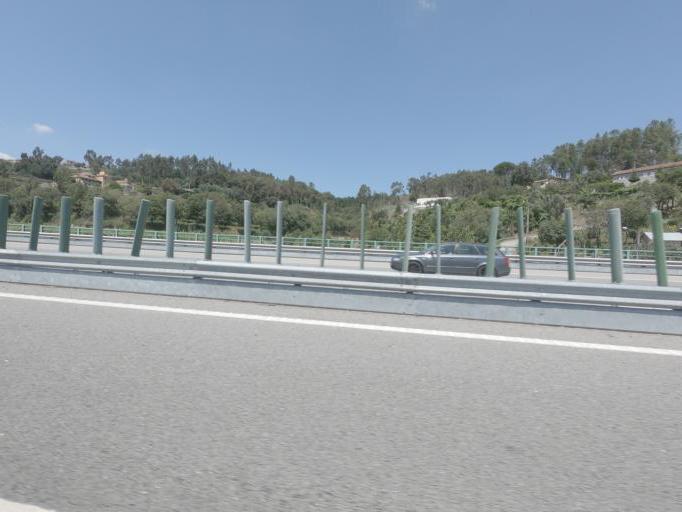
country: PT
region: Porto
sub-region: Marco de Canaveses
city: Marco de Canavezes
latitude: 41.2207
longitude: -8.1593
